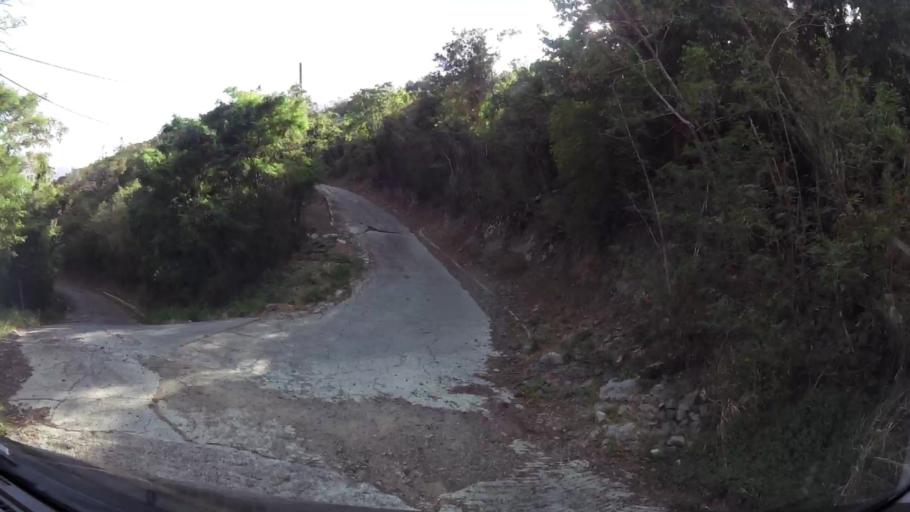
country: VG
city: Road Town
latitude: 18.3944
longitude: -64.6779
